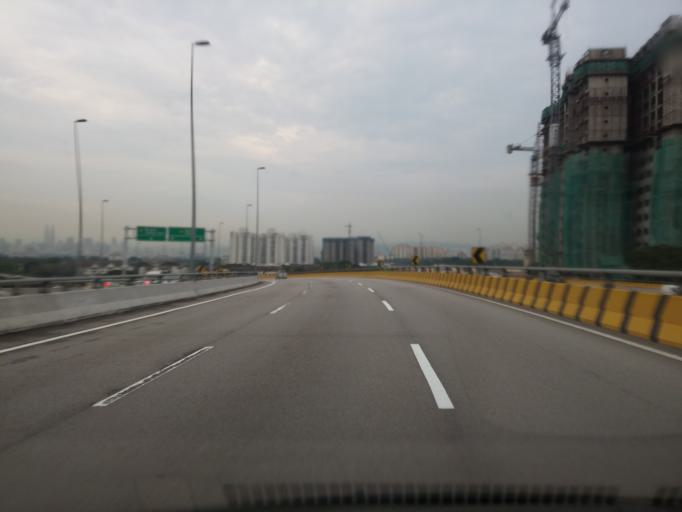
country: MY
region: Kuala Lumpur
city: Kuala Lumpur
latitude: 3.0895
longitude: 101.6958
